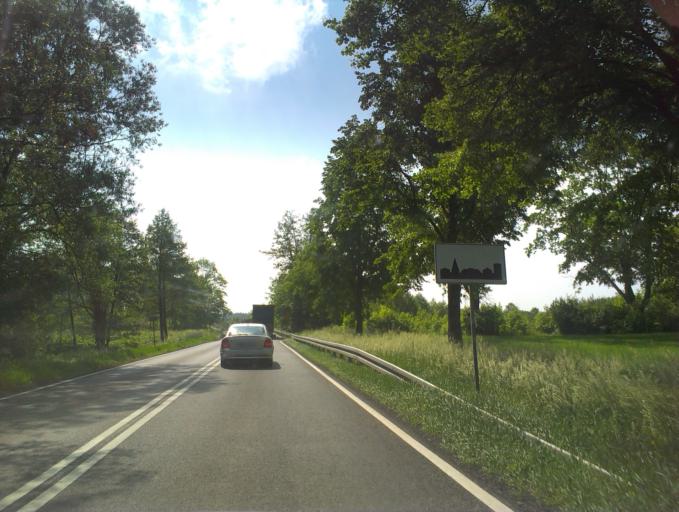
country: PL
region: Greater Poland Voivodeship
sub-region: Powiat zlotowski
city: Okonek
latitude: 53.4790
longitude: 16.8754
